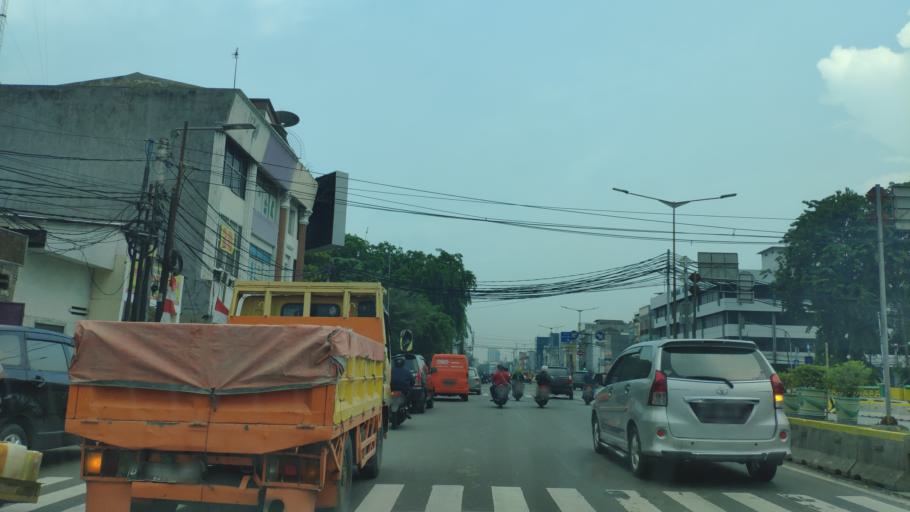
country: ID
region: Jakarta Raya
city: Jakarta
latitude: -6.1710
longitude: 106.8104
